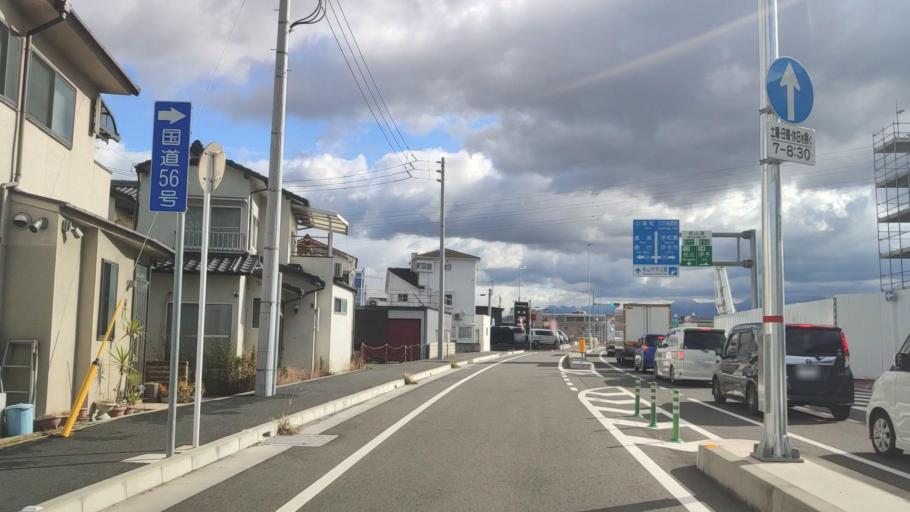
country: JP
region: Ehime
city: Masaki-cho
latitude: 33.8114
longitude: 132.7328
